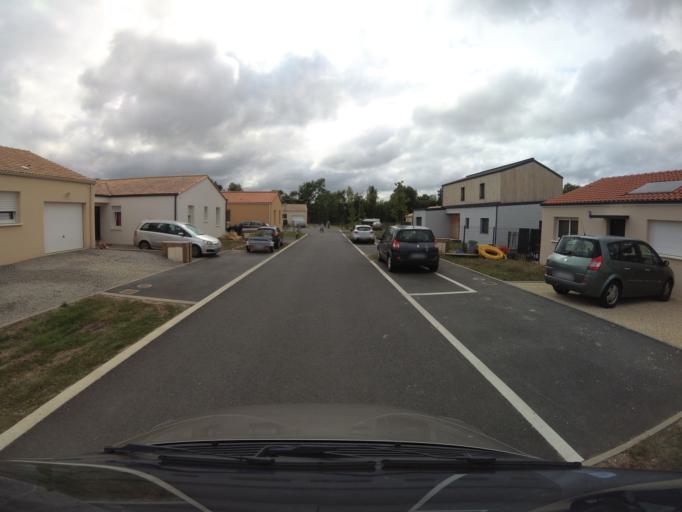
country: FR
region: Pays de la Loire
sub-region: Departement de la Vendee
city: Saint-Philbert-de-Bouaine
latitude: 46.9956
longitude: -1.5234
